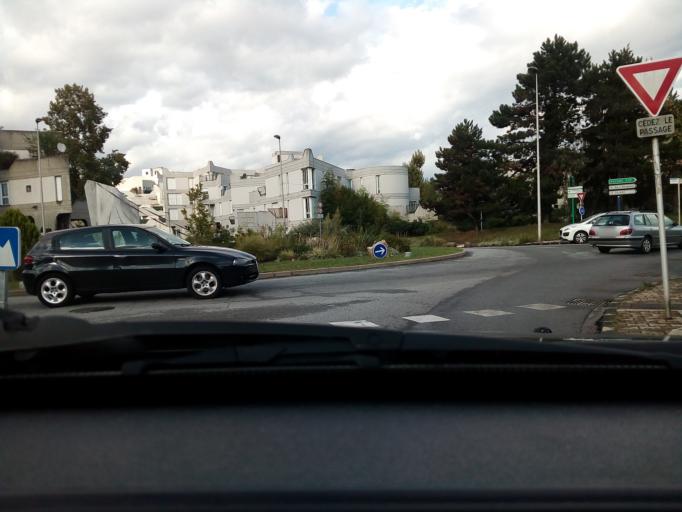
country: FR
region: Rhone-Alpes
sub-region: Departement de l'Isere
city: Saint-Martin-d'Heres
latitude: 45.1683
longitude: 5.7553
